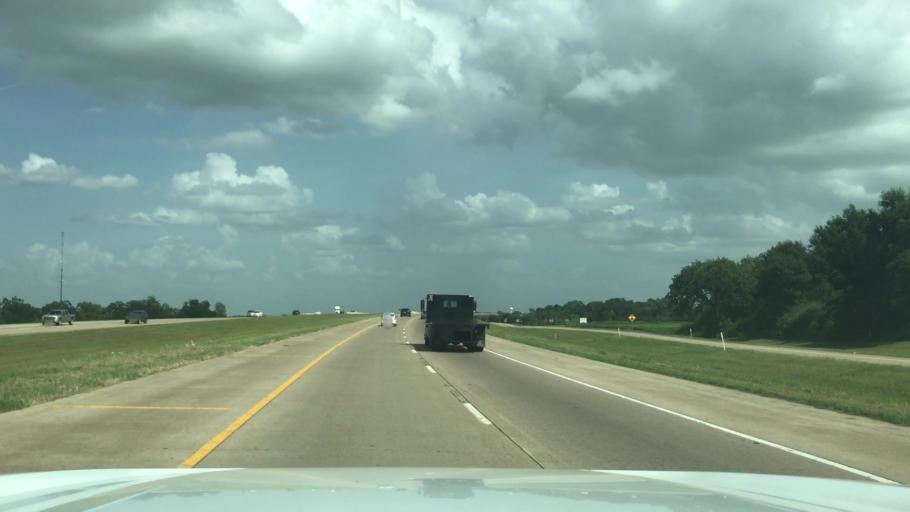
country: US
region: Texas
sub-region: Waller County
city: Prairie View
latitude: 30.0889
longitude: -96.0158
